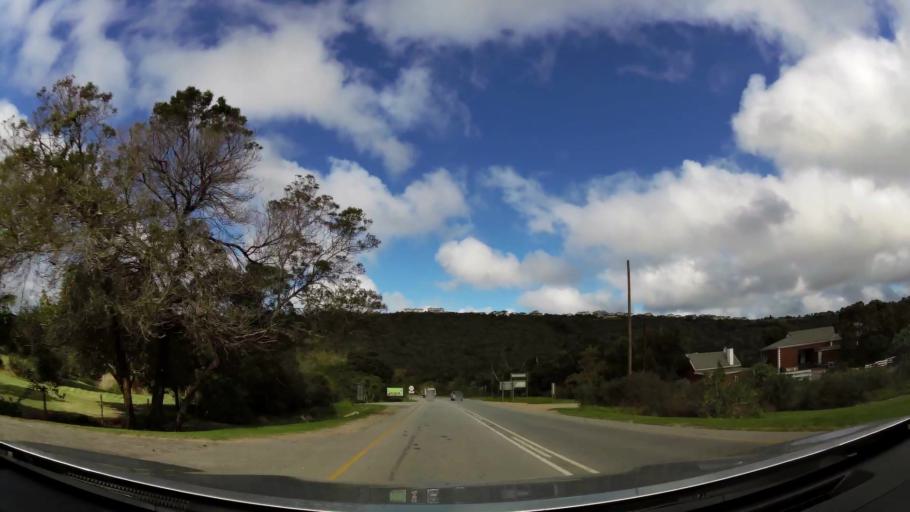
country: ZA
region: Western Cape
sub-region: Eden District Municipality
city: Plettenberg Bay
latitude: -34.0606
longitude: 23.3544
